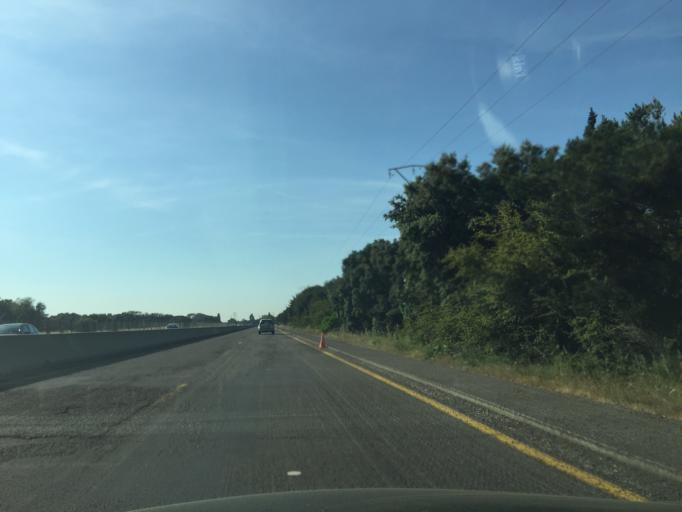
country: FR
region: Provence-Alpes-Cote d'Azur
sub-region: Departement des Bouches-du-Rhone
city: Fos-sur-Mer
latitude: 43.4655
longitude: 4.9153
